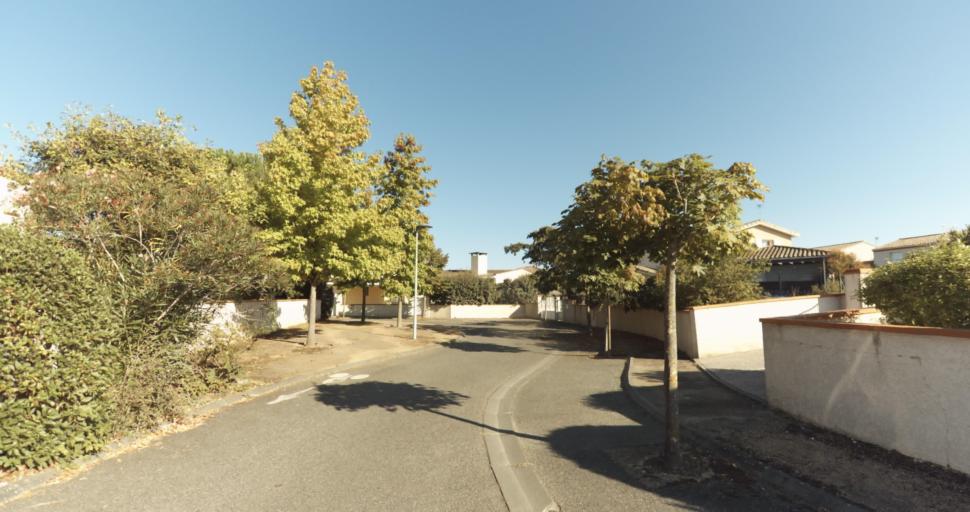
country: FR
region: Midi-Pyrenees
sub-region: Departement de la Haute-Garonne
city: L'Union
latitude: 43.6650
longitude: 1.4878
